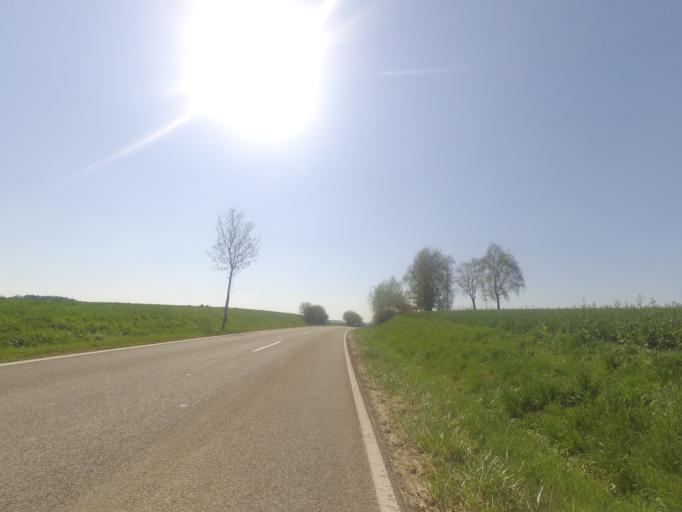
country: DE
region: Bavaria
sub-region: Swabia
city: Pfaffenhofen an der Roth
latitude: 48.3502
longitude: 10.1959
